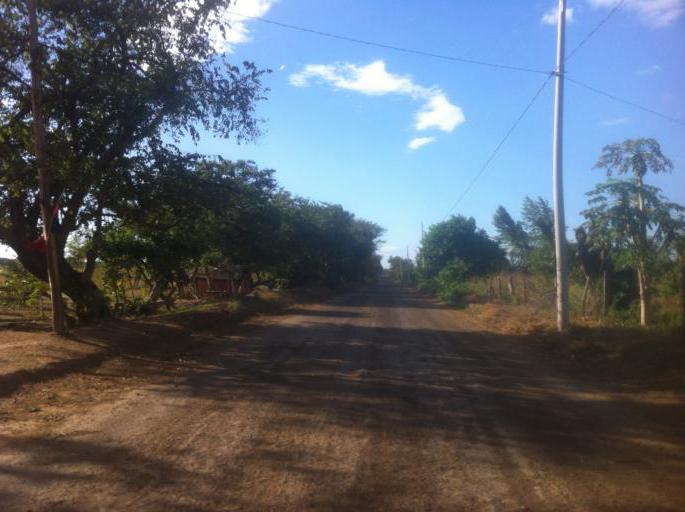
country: NI
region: Managua
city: Masachapa
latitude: 11.8442
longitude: -86.5354
